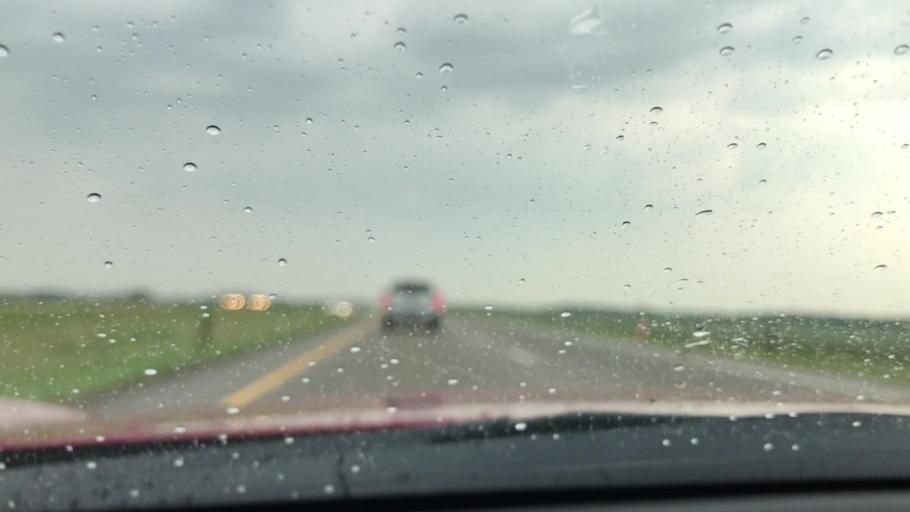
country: CA
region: Alberta
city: Ponoka
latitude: 52.6446
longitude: -113.6640
